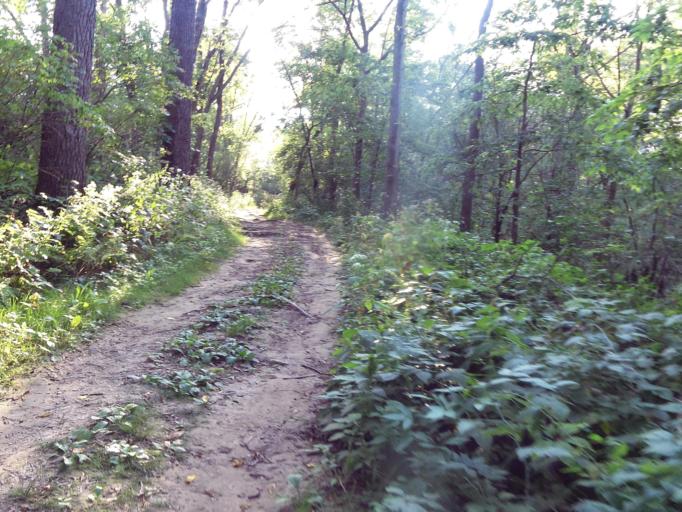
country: US
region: Minnesota
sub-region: Washington County
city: Afton
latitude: 44.8411
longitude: -92.7745
